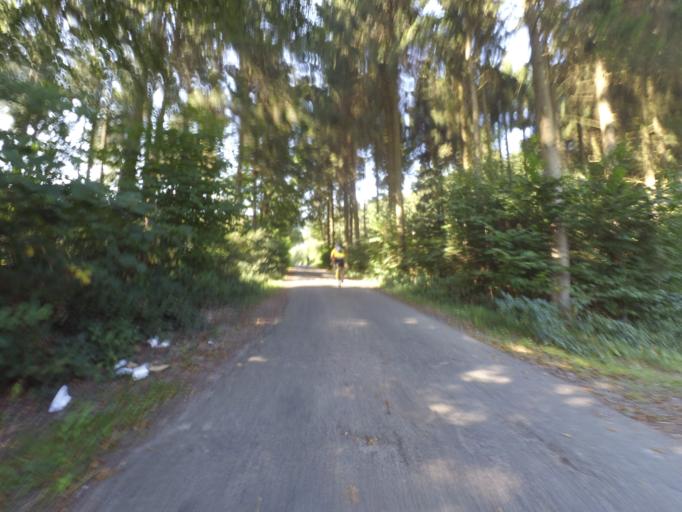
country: DE
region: North Rhine-Westphalia
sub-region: Regierungsbezirk Munster
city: Horstmar
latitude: 52.1009
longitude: 7.2830
